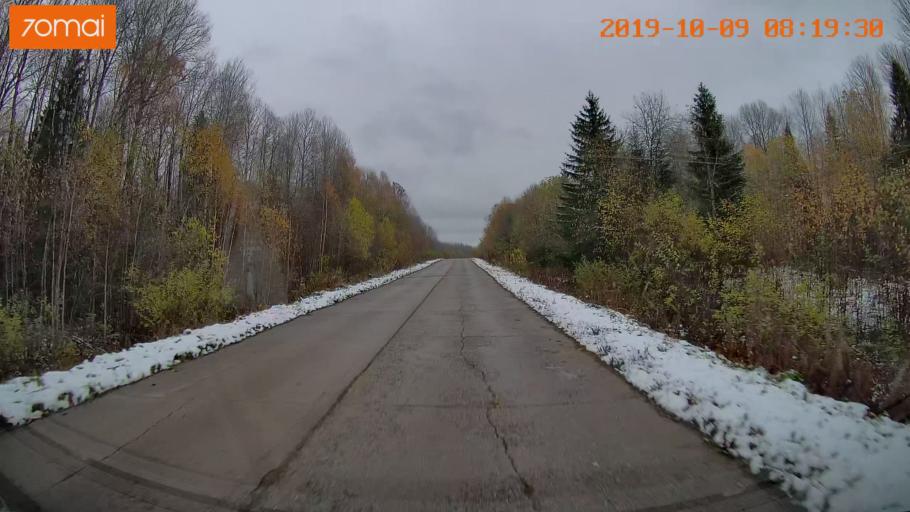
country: RU
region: Vologda
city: Gryazovets
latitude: 58.7421
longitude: 40.2432
